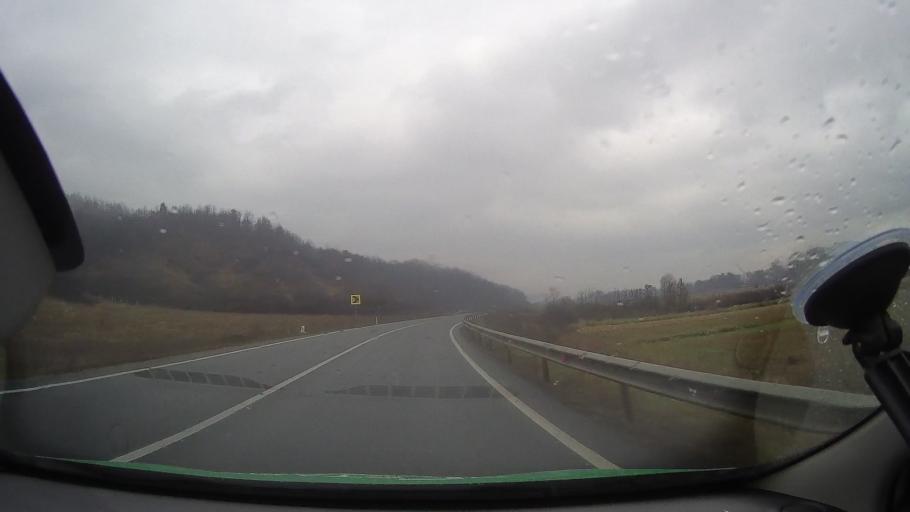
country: RO
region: Hunedoara
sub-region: Comuna Tomesti
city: Tomesti
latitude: 46.1837
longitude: 22.6530
